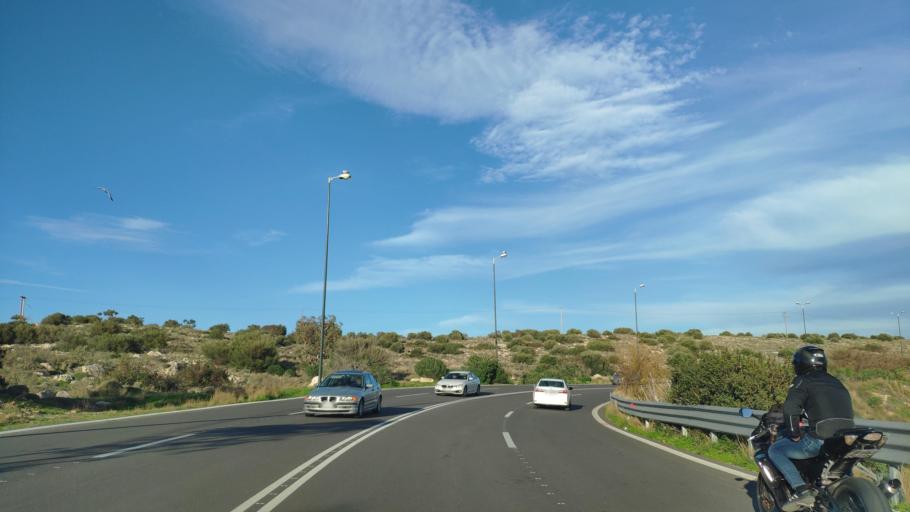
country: GR
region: Attica
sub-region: Nomarchia Anatolikis Attikis
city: Vouliagmeni
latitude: 37.7968
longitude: 23.7923
